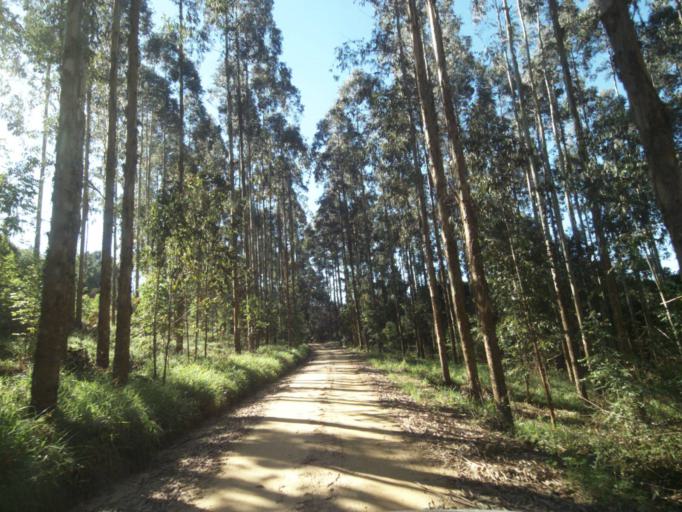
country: BR
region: Parana
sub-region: Tibagi
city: Tibagi
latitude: -24.5573
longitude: -50.4723
